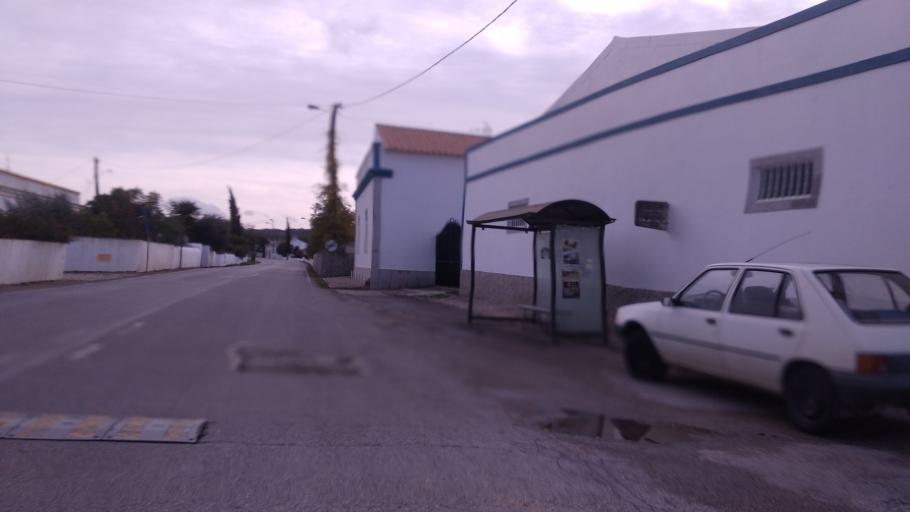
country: PT
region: Faro
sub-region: Sao Bras de Alportel
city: Sao Bras de Alportel
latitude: 37.1746
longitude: -7.9091
